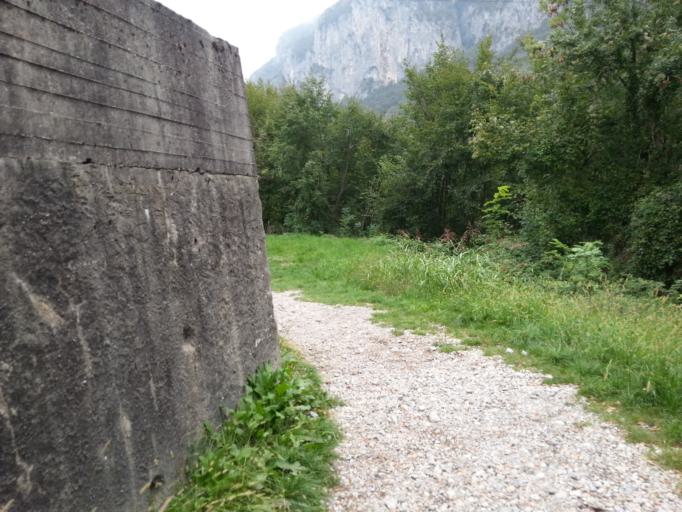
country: IT
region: Lombardy
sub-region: Provincia di Lecco
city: Ballabio
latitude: 45.8628
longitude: 9.4289
